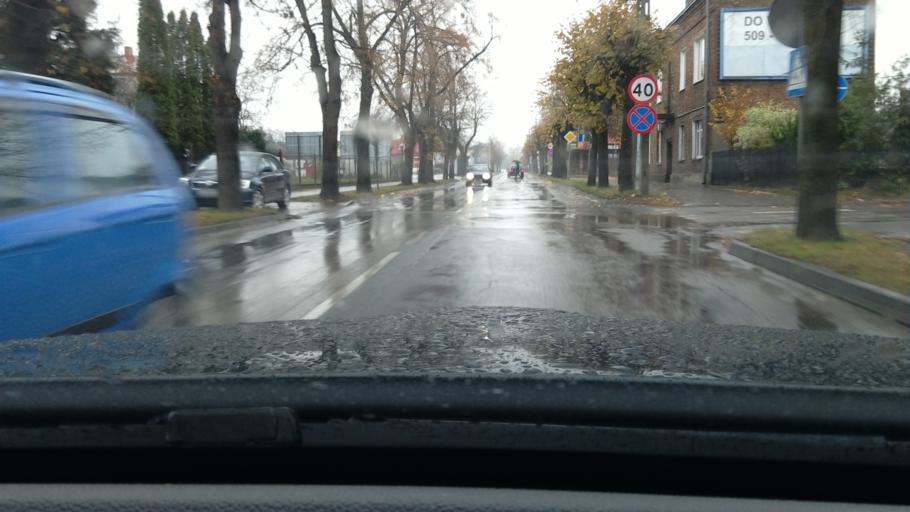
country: PL
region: Lodz Voivodeship
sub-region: Skierniewice
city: Skierniewice
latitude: 51.9534
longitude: 20.1371
